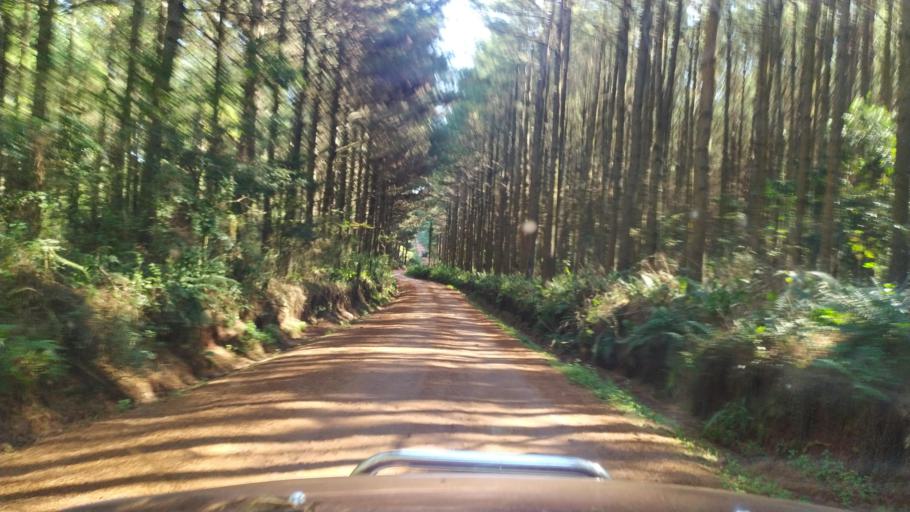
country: AR
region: Misiones
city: El Alcazar
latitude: -26.7356
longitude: -54.6522
